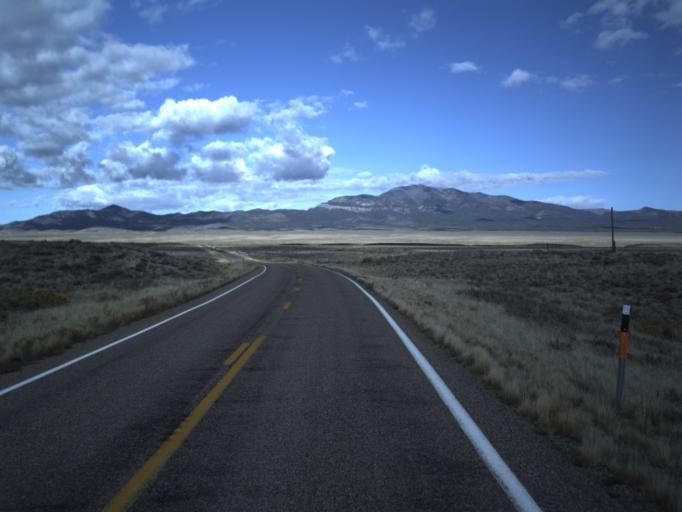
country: US
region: Utah
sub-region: Beaver County
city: Milford
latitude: 38.4331
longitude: -113.1324
